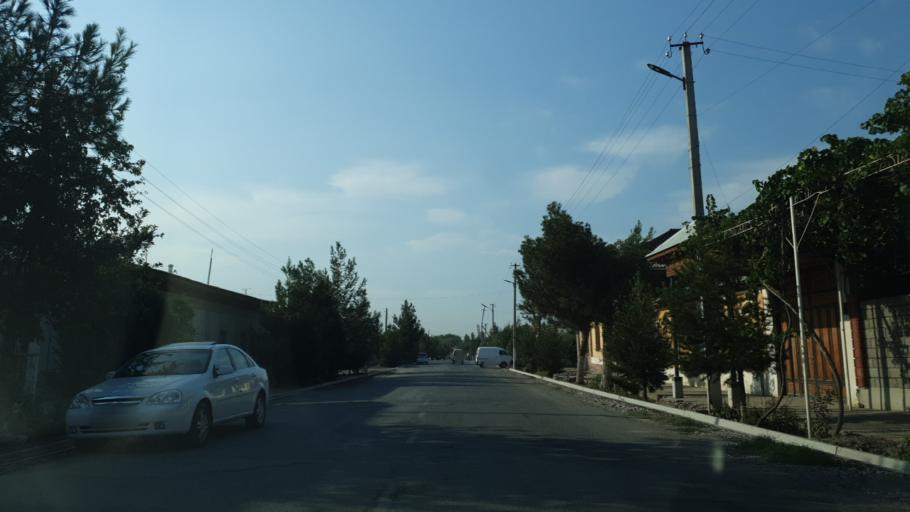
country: UZ
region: Fergana
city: Yaypan
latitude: 40.3717
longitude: 70.8132
